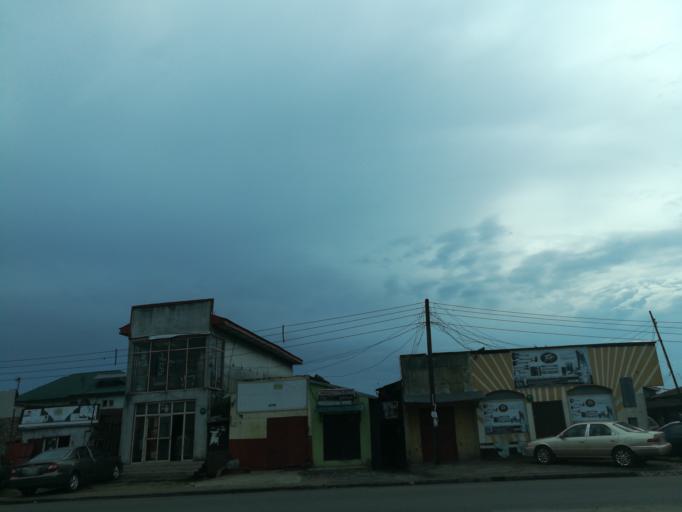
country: NG
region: Rivers
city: Port Harcourt
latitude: 4.7995
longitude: 7.0060
